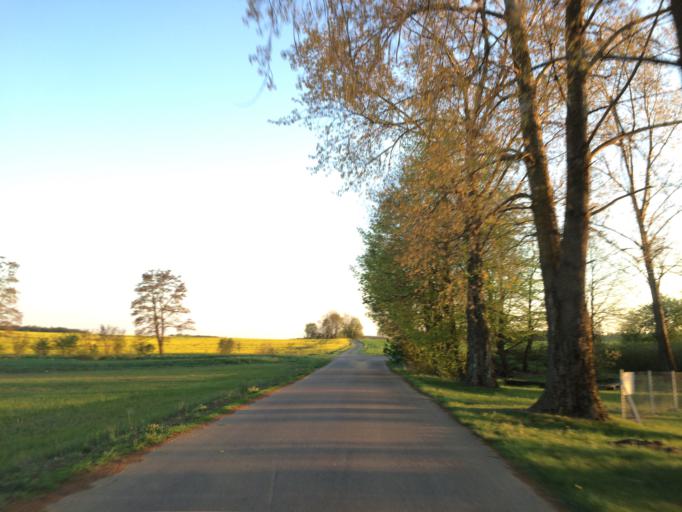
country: PL
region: Warmian-Masurian Voivodeship
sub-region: Powiat dzialdowski
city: Rybno
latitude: 53.4448
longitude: 19.9013
